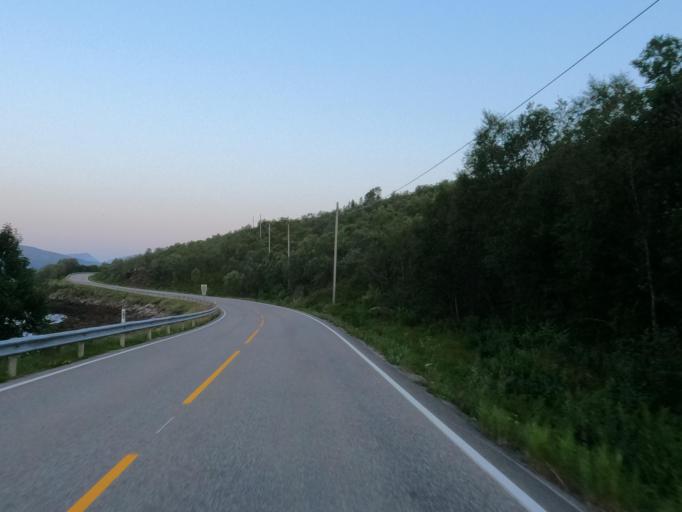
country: NO
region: Nordland
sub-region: Lodingen
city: Lodingen
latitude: 68.5005
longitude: 16.0942
